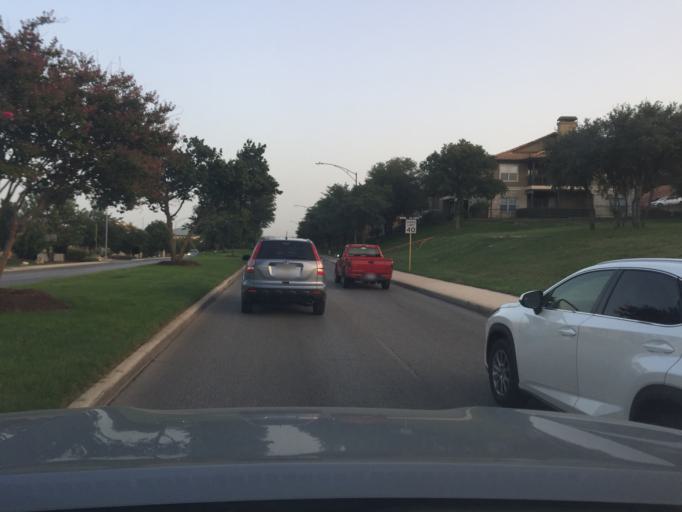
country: US
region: Texas
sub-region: Bexar County
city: Hollywood Park
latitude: 29.6322
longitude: -98.4956
